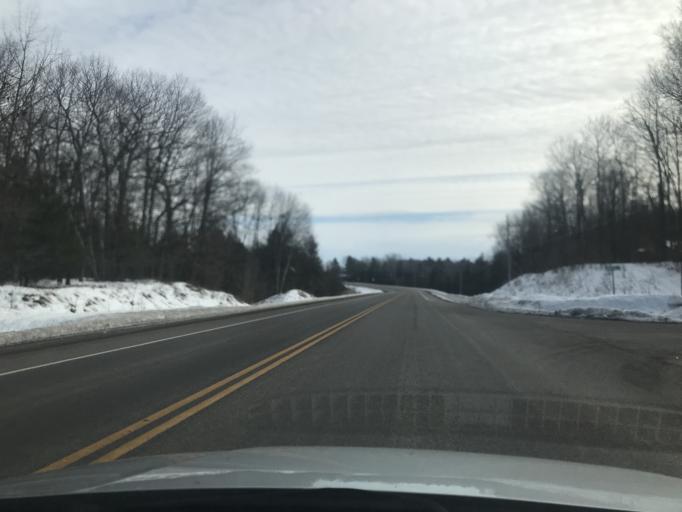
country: US
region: Wisconsin
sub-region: Oconto County
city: Oconto Falls
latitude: 44.8889
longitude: -88.1658
